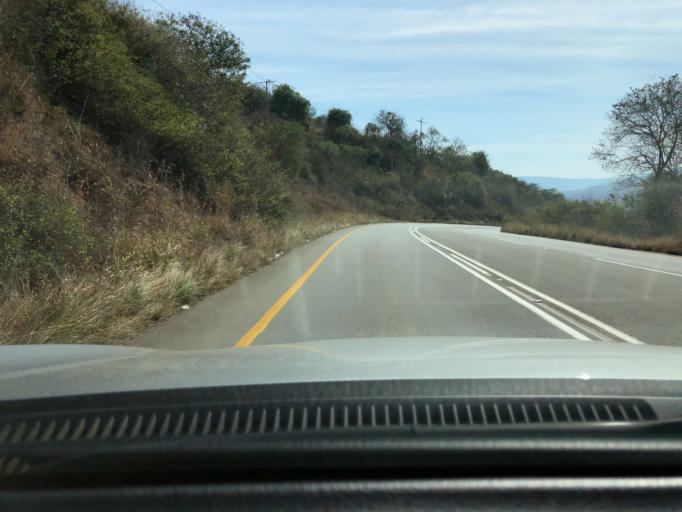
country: ZA
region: KwaZulu-Natal
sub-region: uMgungundlovu District Municipality
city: Richmond
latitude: -29.9905
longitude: 30.2466
